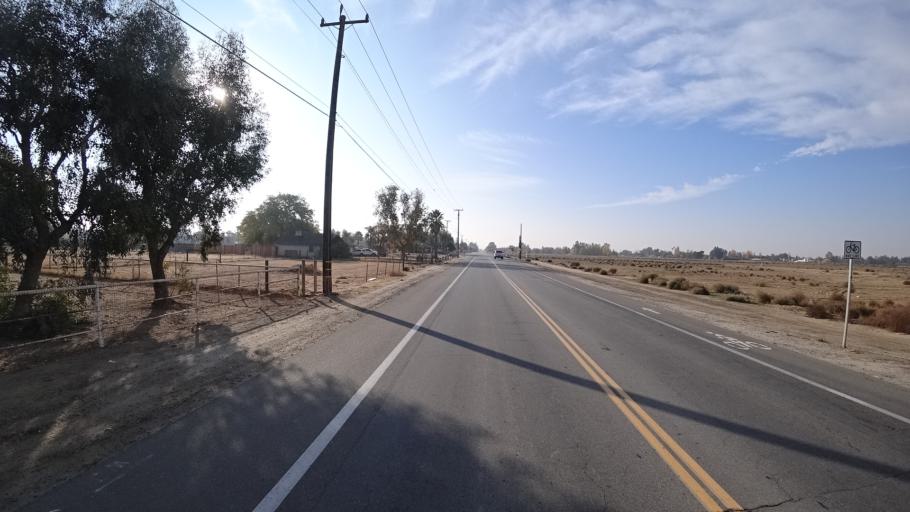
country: US
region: California
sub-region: Kern County
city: Rosedale
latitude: 35.3701
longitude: -119.1633
